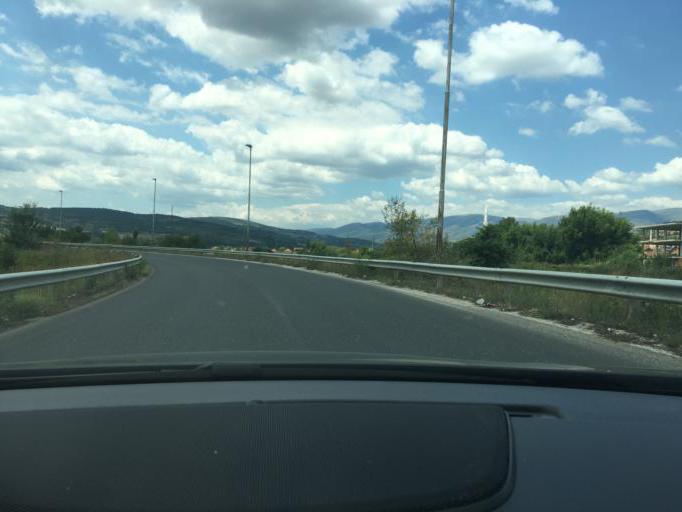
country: MK
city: Kondovo
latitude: 42.0088
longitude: 21.3228
